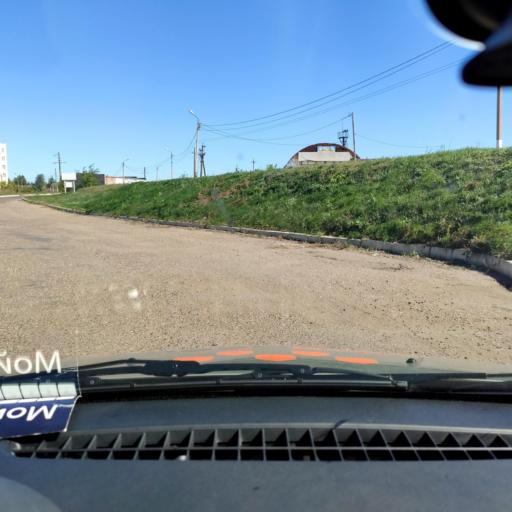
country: RU
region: Bashkortostan
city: Kumertau
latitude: 52.7713
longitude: 55.7957
